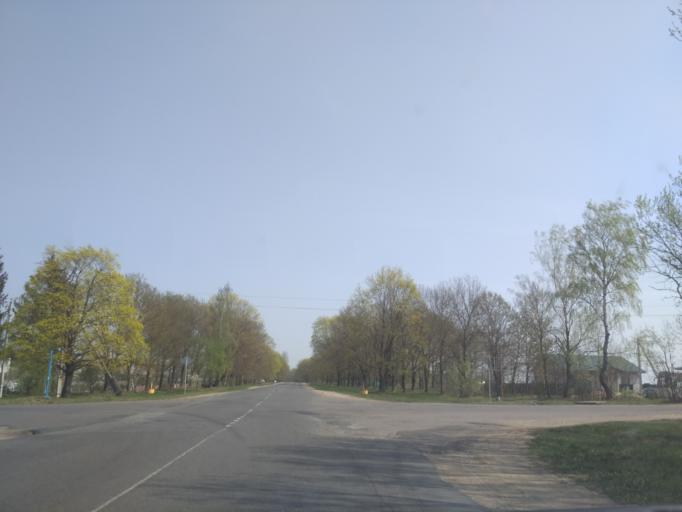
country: BY
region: Minsk
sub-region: Smalyavitski Rayon
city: Oktjabr'skij
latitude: 54.0285
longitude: 28.2072
